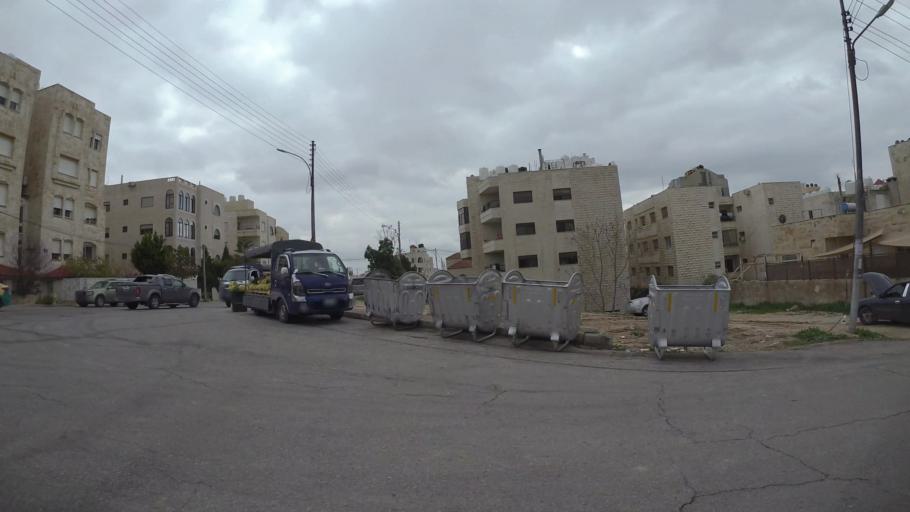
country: JO
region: Amman
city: Wadi as Sir
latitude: 31.9659
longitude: 35.8340
